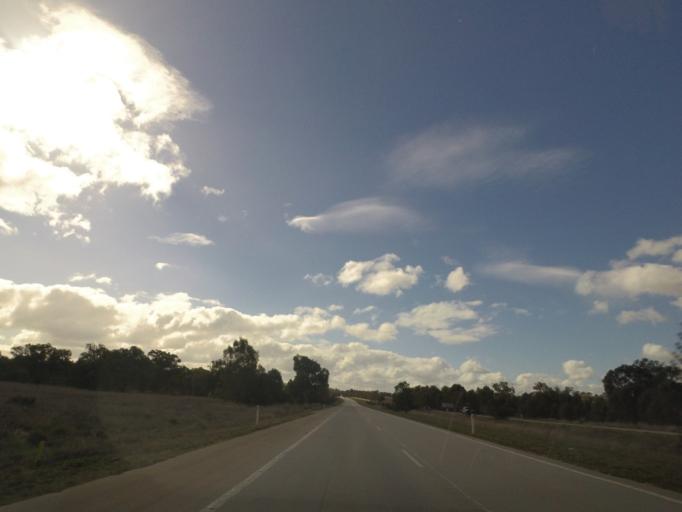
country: AU
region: New South Wales
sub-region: Albury Municipality
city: Lavington
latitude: -36.0074
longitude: 146.9894
